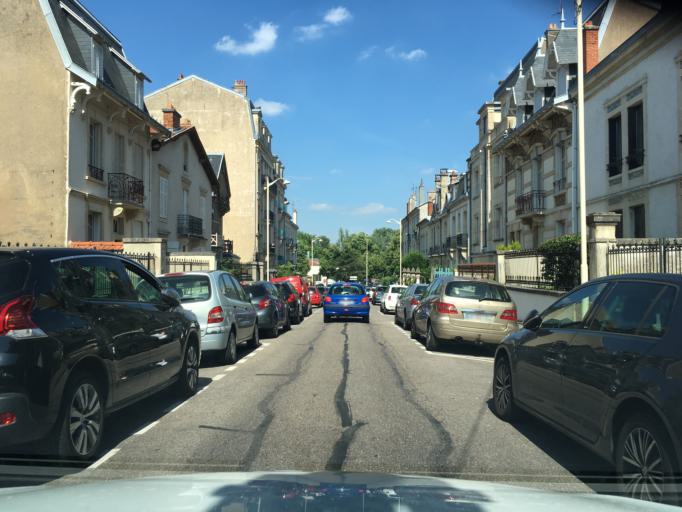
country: FR
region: Lorraine
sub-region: Departement de Meurthe-et-Moselle
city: Villers-les-Nancy
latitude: 48.6782
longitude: 6.1662
